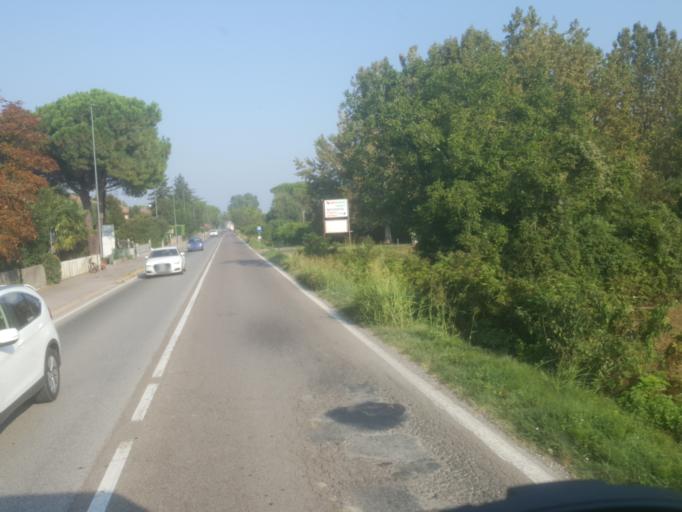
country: IT
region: Emilia-Romagna
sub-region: Provincia di Ravenna
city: Mezzano
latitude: 44.4612
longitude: 12.0964
